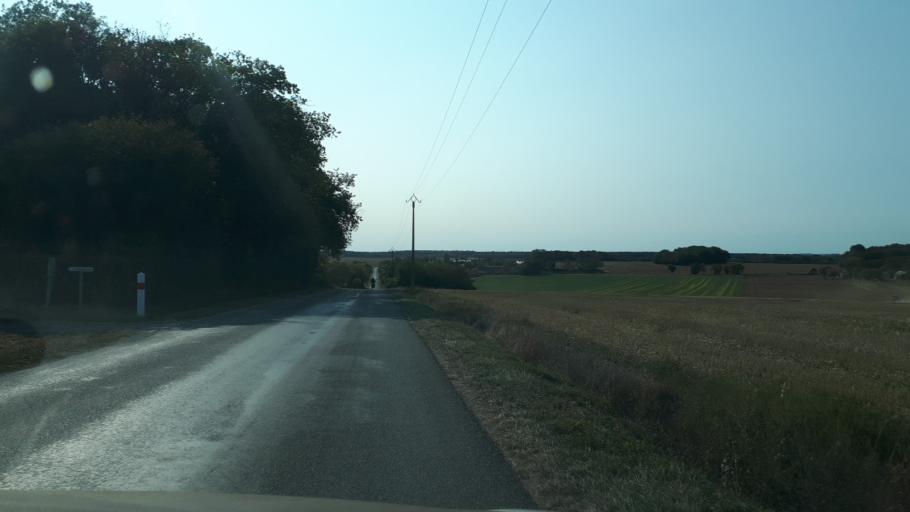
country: FR
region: Centre
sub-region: Departement du Cher
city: Rians
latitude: 47.1843
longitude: 2.6870
